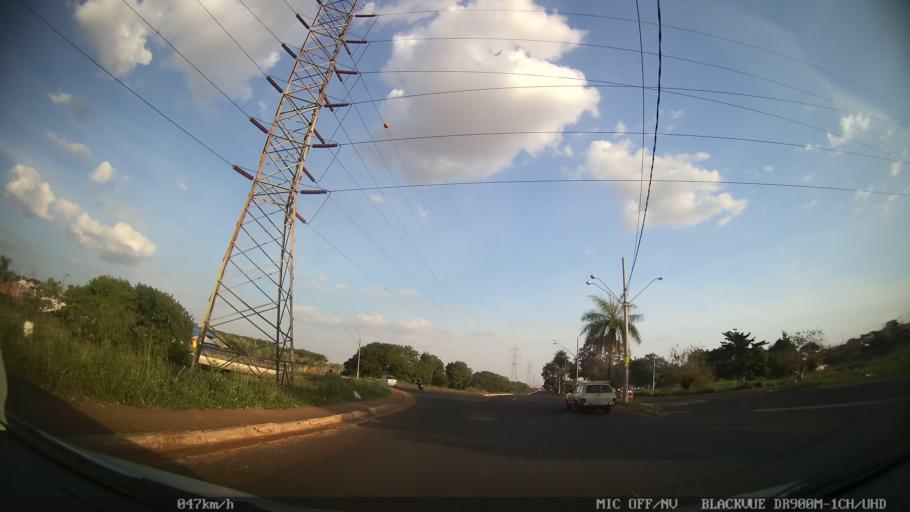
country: BR
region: Sao Paulo
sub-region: Ribeirao Preto
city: Ribeirao Preto
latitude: -21.1201
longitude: -47.8030
